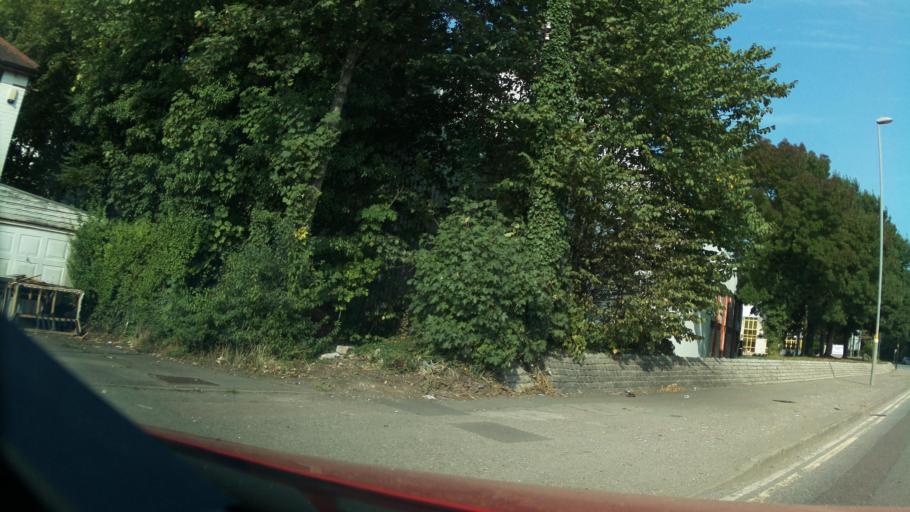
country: GB
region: England
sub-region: Warwickshire
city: Curdworth
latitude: 52.5293
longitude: -1.7629
